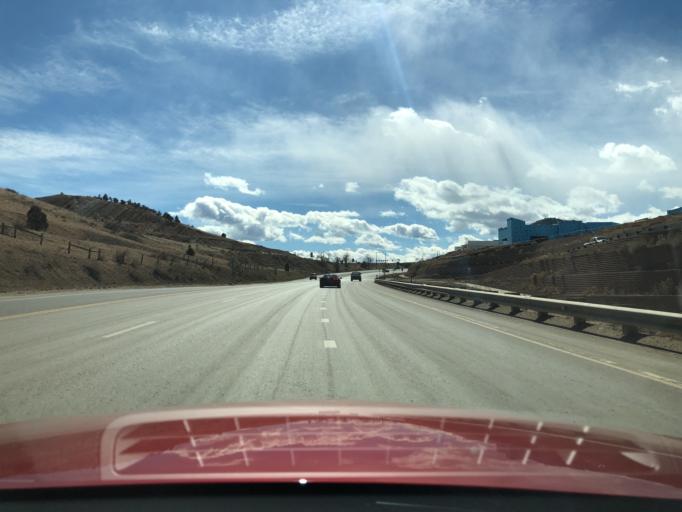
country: US
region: Colorado
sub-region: Jefferson County
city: West Pleasant View
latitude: 39.7053
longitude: -105.2040
